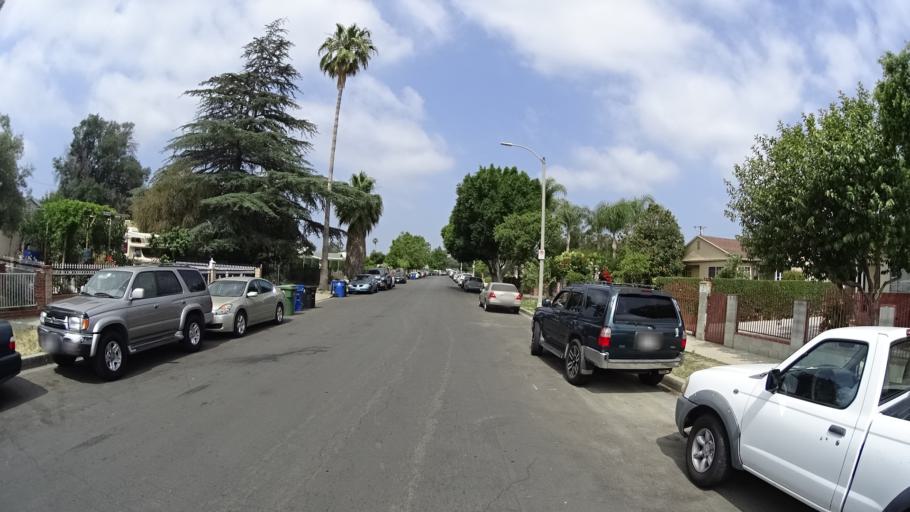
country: US
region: California
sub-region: Los Angeles County
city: Van Nuys
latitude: 34.1857
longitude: -118.4597
